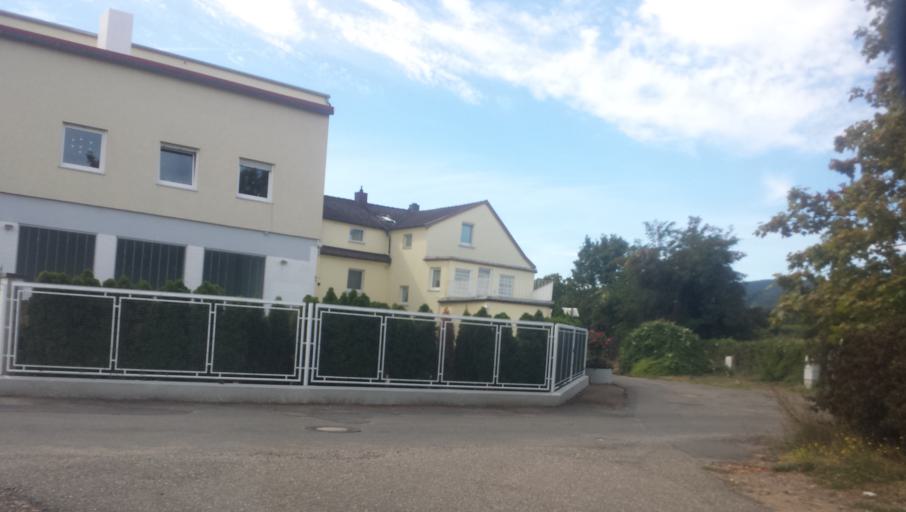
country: DE
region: Rheinland-Pfalz
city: Neustadt
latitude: 49.3314
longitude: 8.1415
